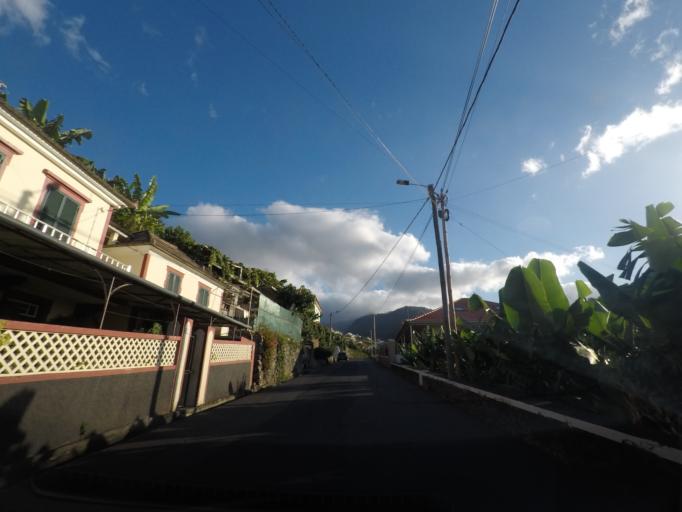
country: PT
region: Madeira
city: Ponta do Sol
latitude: 32.6834
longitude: -17.0972
